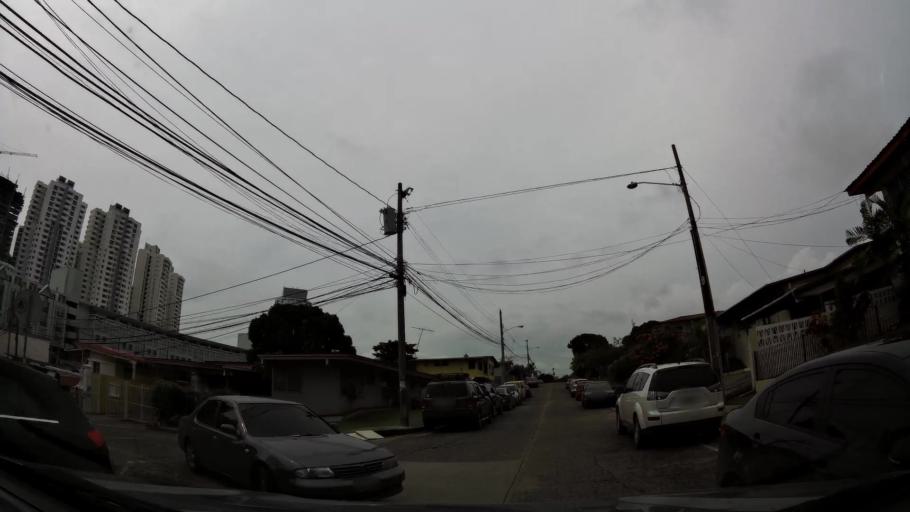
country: PA
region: Panama
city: Panama
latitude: 8.9970
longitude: -79.5314
